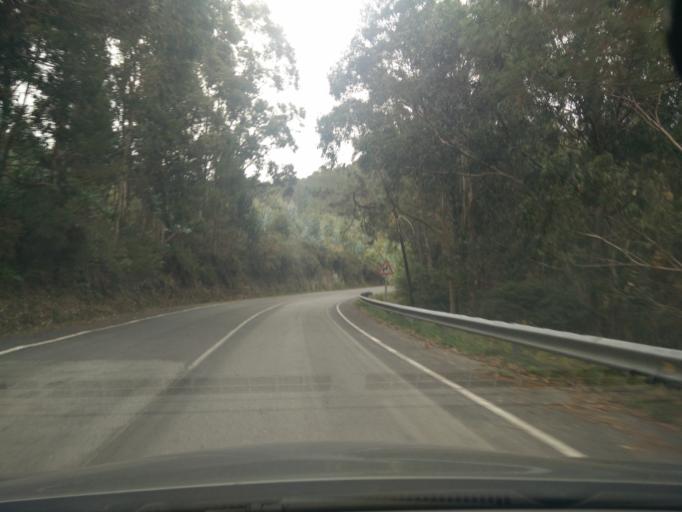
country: ES
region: Galicia
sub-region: Provincia da Coruna
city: Laxe
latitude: 43.2477
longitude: -8.9382
